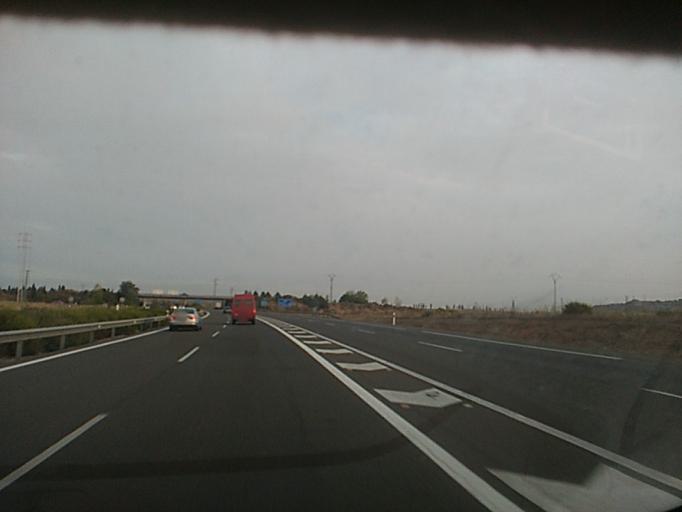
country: ES
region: Castille and Leon
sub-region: Provincia de Valladolid
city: Tordesillas
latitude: 41.5091
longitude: -4.9888
